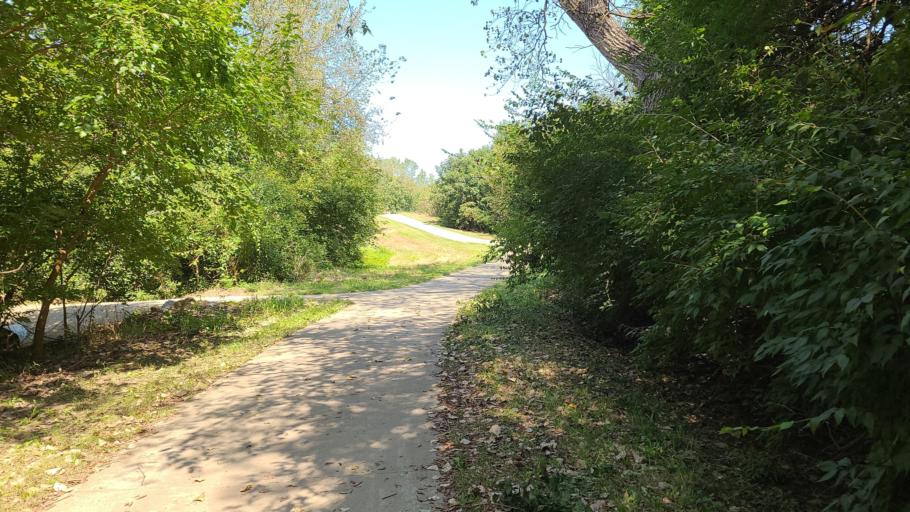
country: US
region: Kansas
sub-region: Douglas County
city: Lawrence
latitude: 38.9633
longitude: -95.3241
